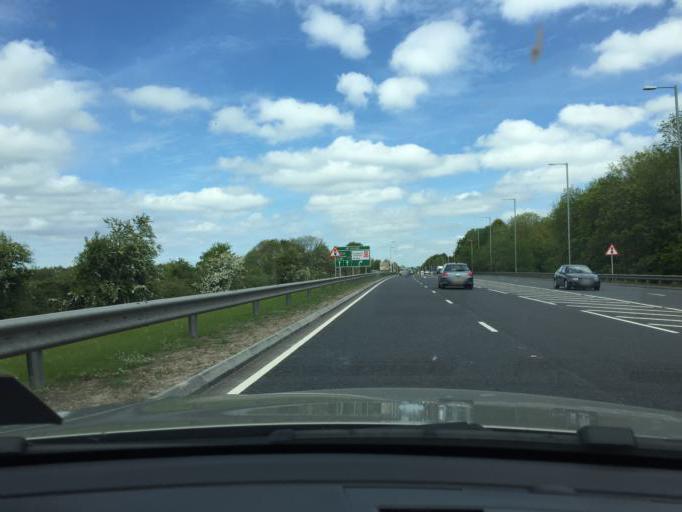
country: GB
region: Northern Ireland
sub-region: Armagh District
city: Portadown
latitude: 54.4326
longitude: -6.4328
